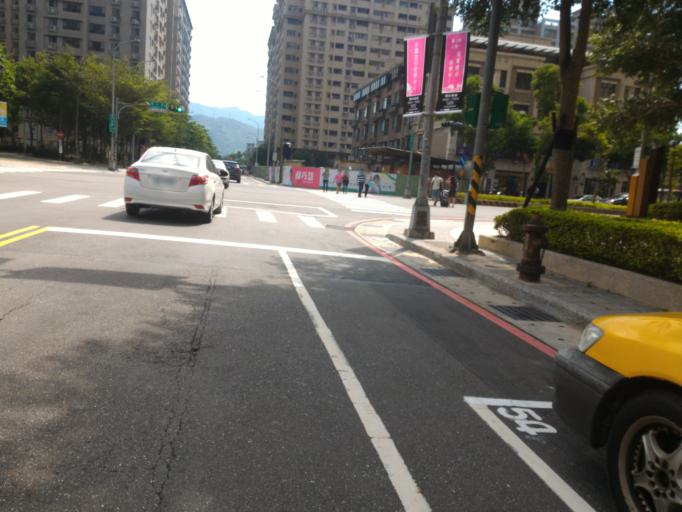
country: TW
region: Taiwan
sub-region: Taoyuan
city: Taoyuan
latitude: 24.9465
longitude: 121.3822
